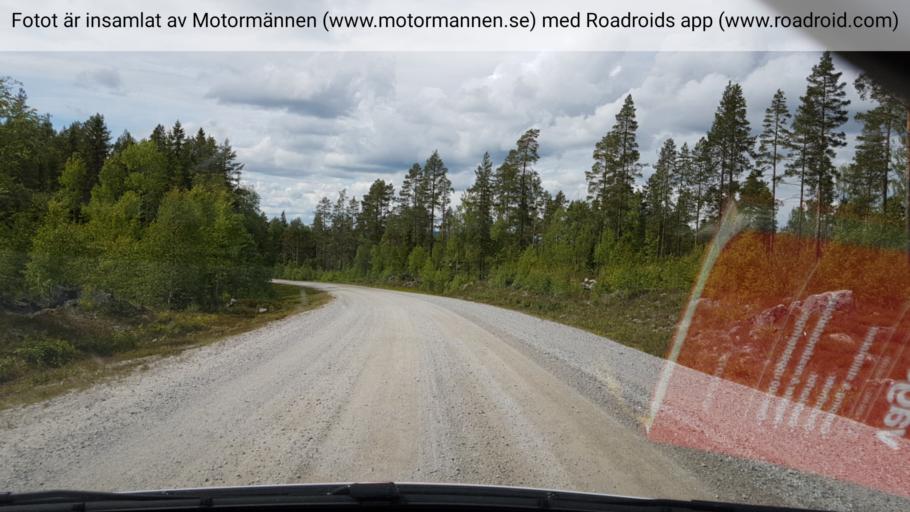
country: SE
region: Vaesternorrland
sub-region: Solleftea Kommun
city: Solleftea
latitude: 63.3247
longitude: 17.3646
